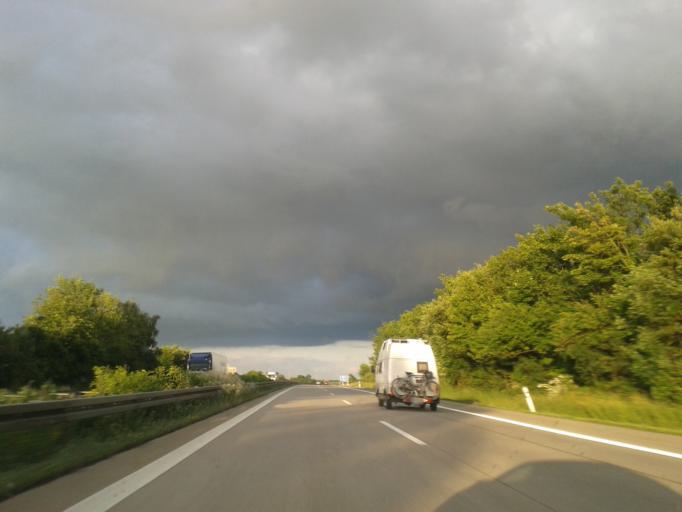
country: DE
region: Saxony
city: Nossen
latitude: 51.0885
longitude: 13.2539
